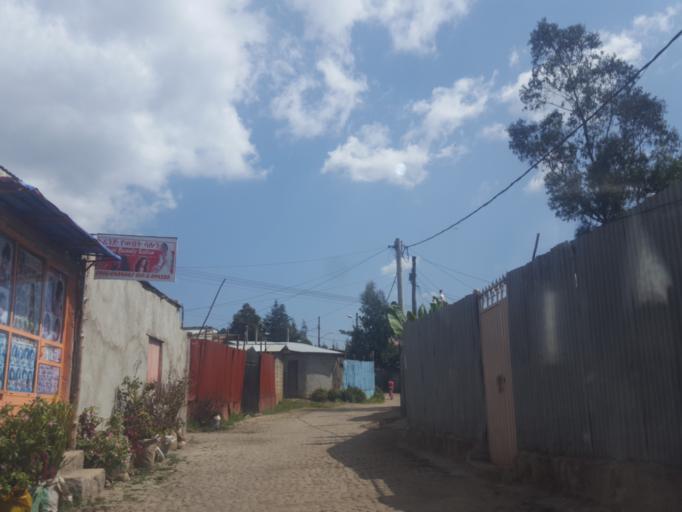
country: ET
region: Adis Abeba
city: Addis Ababa
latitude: 9.0574
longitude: 38.7283
